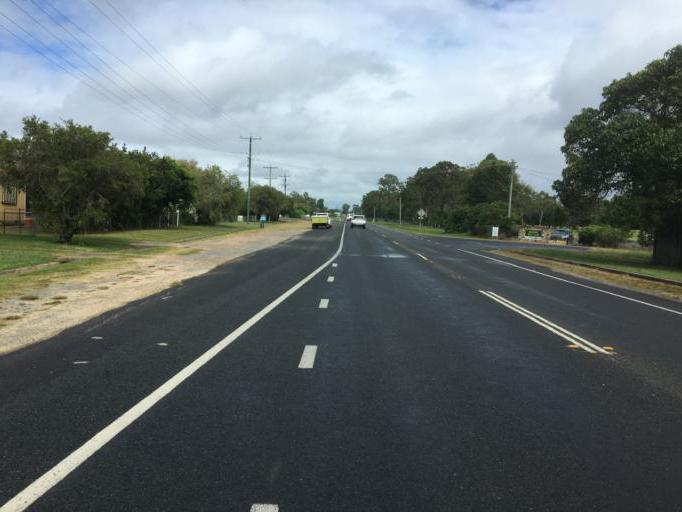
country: AU
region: Queensland
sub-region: Tablelands
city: Mareeba
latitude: -16.9857
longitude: 145.4171
